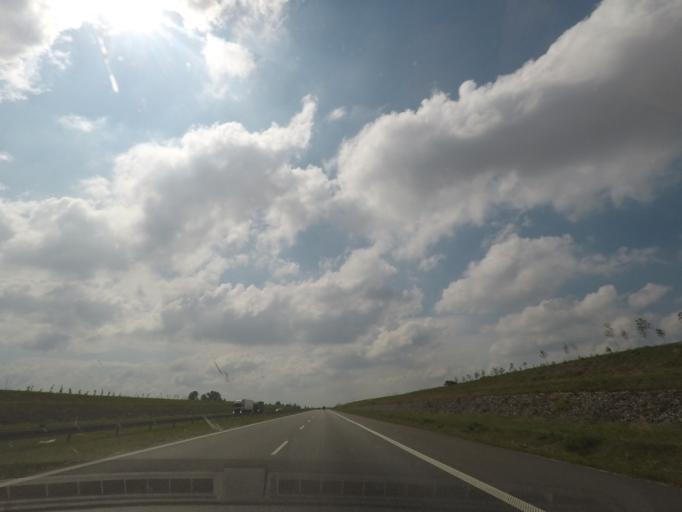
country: PL
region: Lodz Voivodeship
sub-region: Powiat kutnowski
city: Krzyzanow
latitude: 52.1682
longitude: 19.4844
